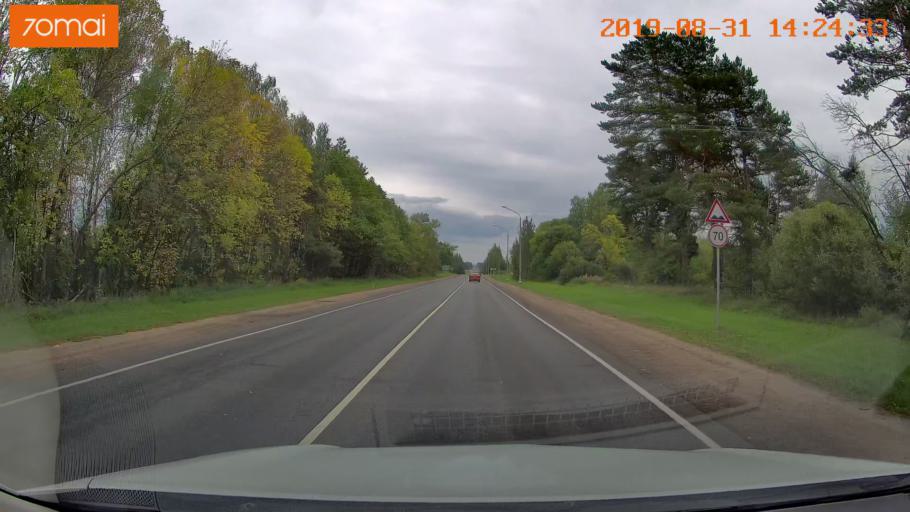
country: RU
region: Smolensk
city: Yekimovichi
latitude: 54.1036
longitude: 33.2575
